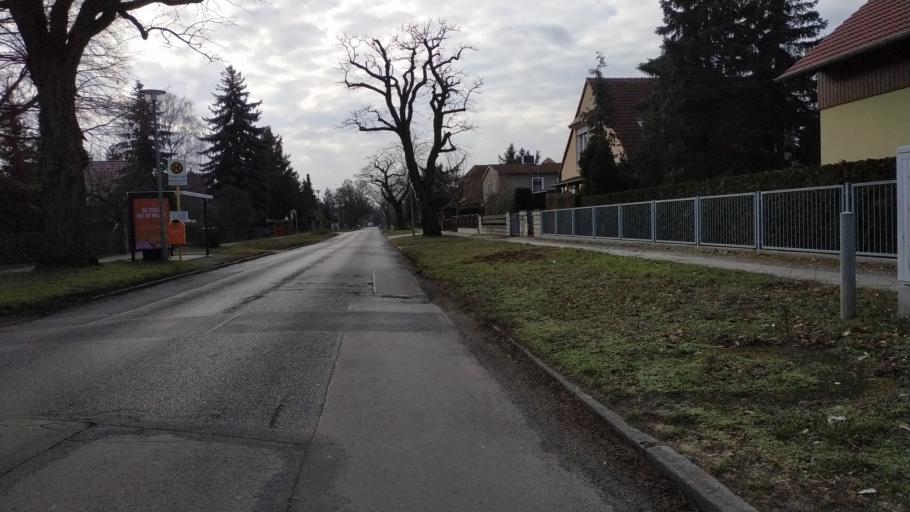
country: DE
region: Berlin
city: Hellersdorf
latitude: 52.5242
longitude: 13.6062
